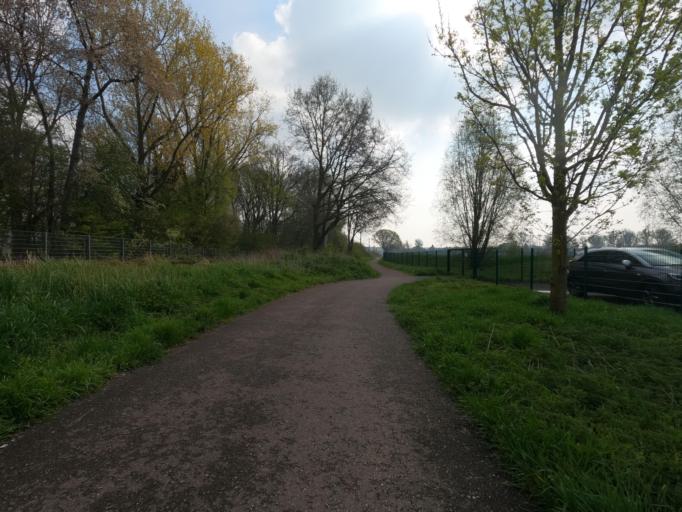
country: DE
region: North Rhine-Westphalia
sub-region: Regierungsbezirk Koln
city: Heinsberg
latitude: 51.0562
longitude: 6.1259
